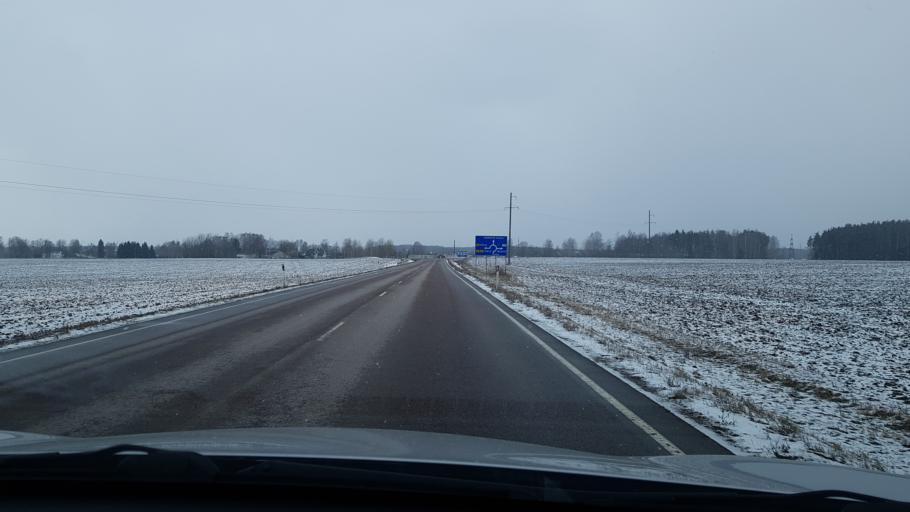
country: EE
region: Polvamaa
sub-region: Polva linn
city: Polva
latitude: 58.0896
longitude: 27.1014
